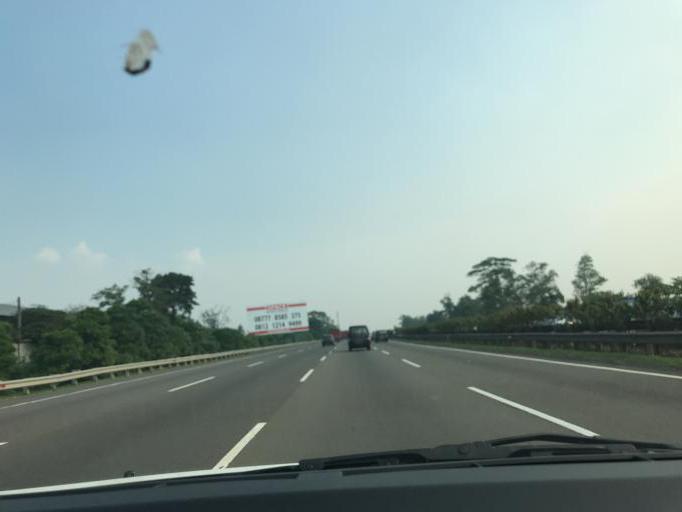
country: ID
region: West Java
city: Citeureup
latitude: -6.5009
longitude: 106.8675
